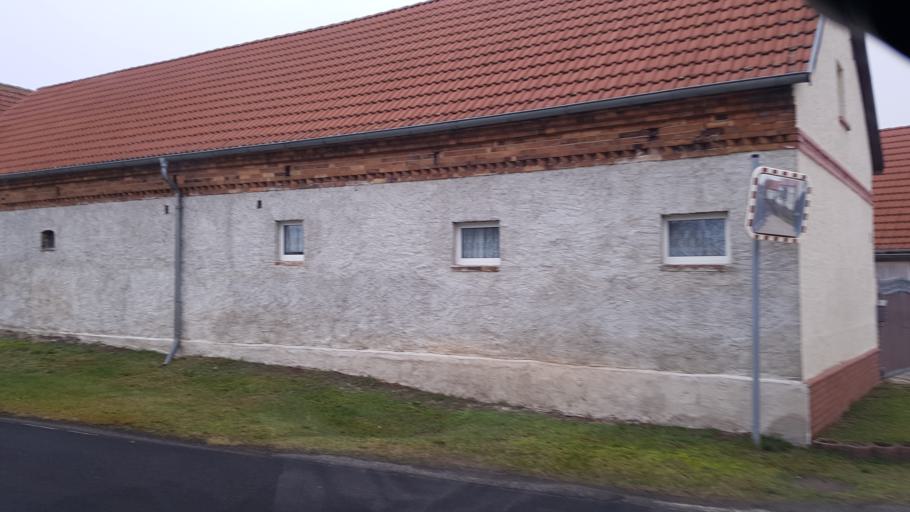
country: DE
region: Brandenburg
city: Bronkow
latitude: 51.6861
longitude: 13.9469
